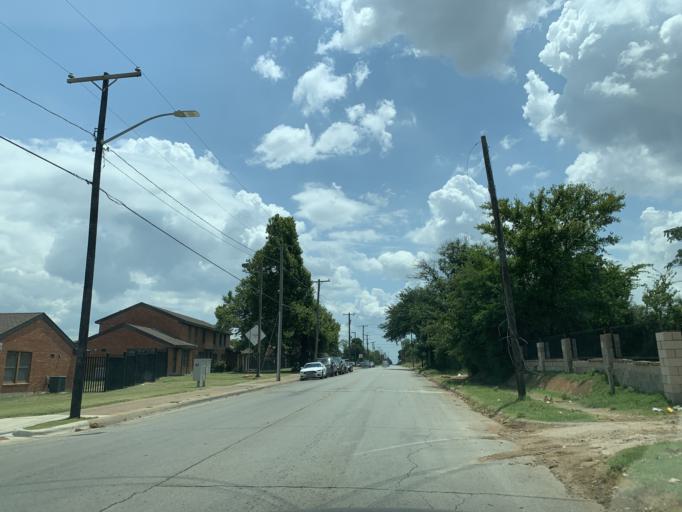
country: US
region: Texas
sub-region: Tarrant County
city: Forest Hill
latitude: 32.7302
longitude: -97.2499
